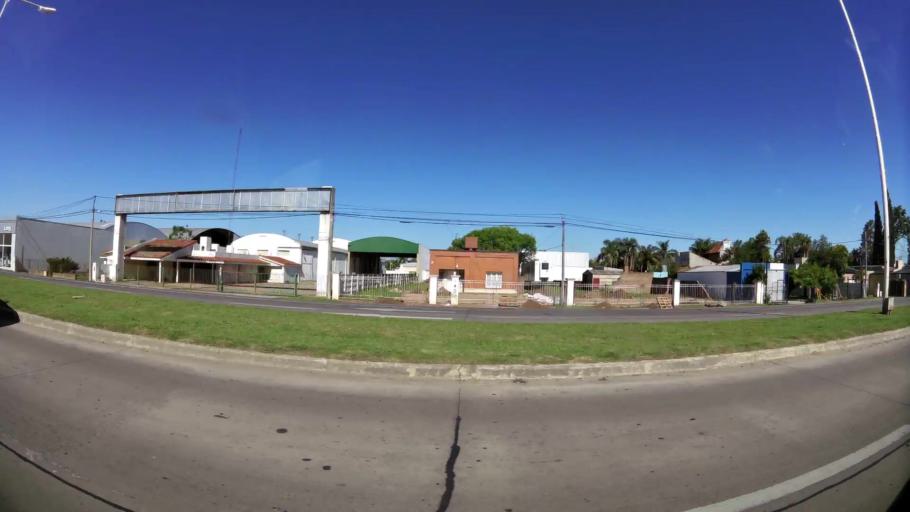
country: AR
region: Santa Fe
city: Rafaela
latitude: -31.2565
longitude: -61.5062
